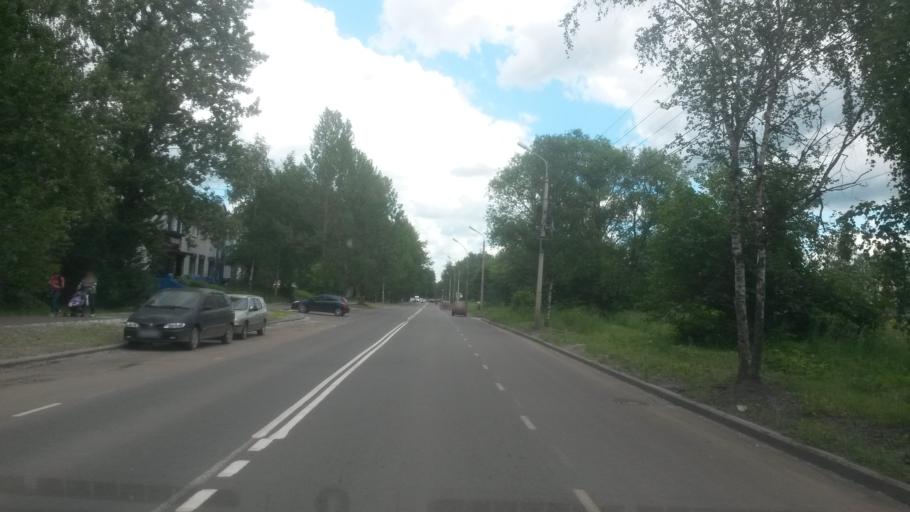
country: RU
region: Jaroslavl
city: Yaroslavl
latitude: 57.6837
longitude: 39.8117
